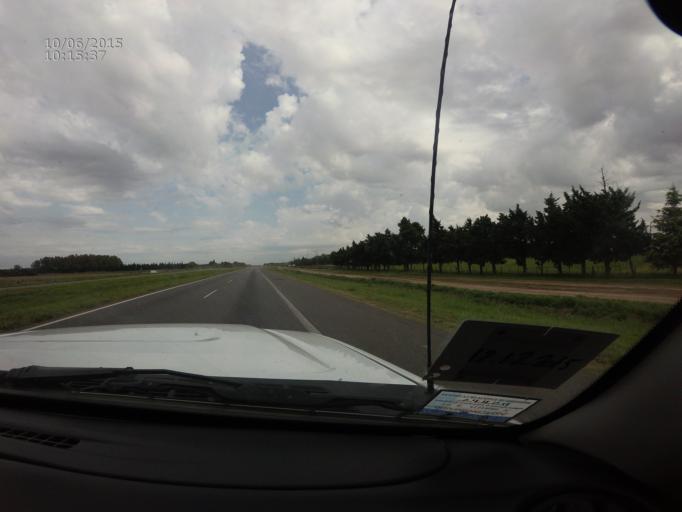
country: AR
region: Buenos Aires
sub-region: Partido de San Pedro
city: San Pedro
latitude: -33.7593
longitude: -59.7363
